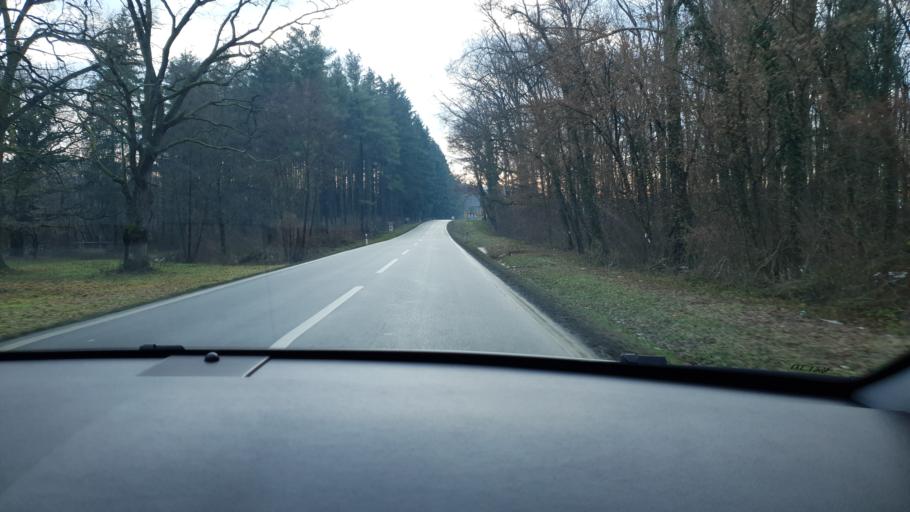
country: HR
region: Pozesko-Slavonska
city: Vidovci
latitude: 45.3501
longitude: 17.7213
